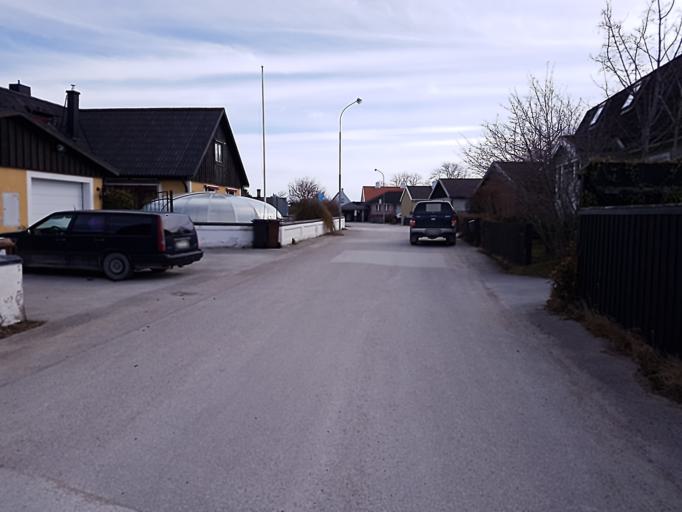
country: SE
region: Gotland
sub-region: Gotland
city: Visby
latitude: 57.6346
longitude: 18.3177
